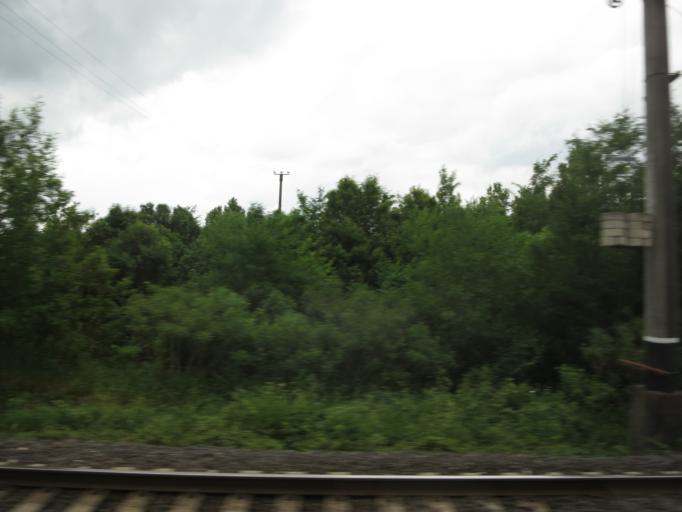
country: GE
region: Imereti
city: Vani
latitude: 42.1893
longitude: 42.4815
